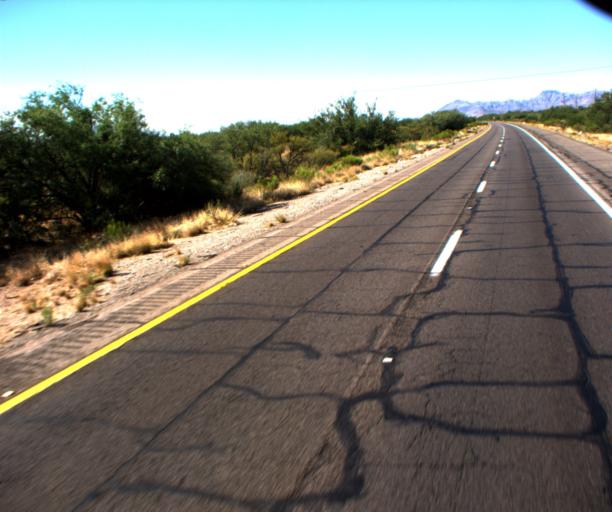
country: US
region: Arizona
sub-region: Pima County
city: Arivaca Junction
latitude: 31.7122
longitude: -111.0644
